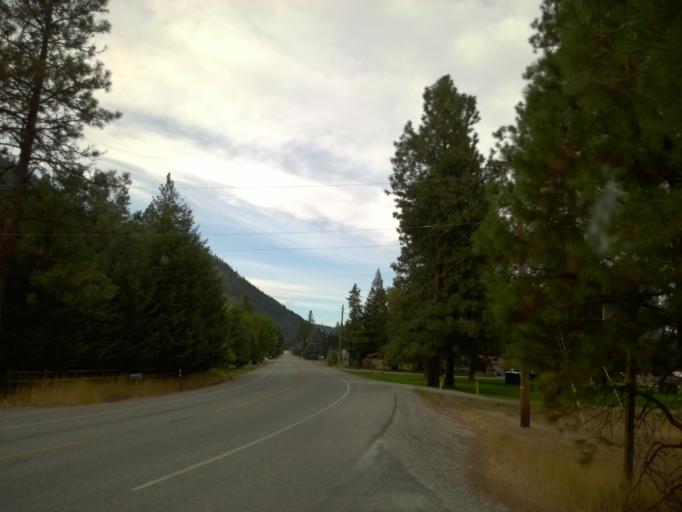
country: US
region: Washington
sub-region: Chelan County
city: Leavenworth
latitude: 47.5543
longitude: -120.6801
